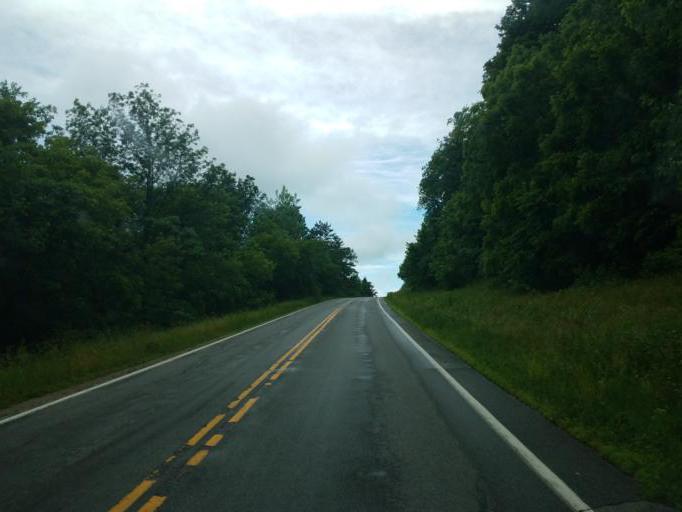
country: US
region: Wisconsin
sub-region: Vernon County
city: Hillsboro
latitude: 43.6604
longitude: -90.4114
